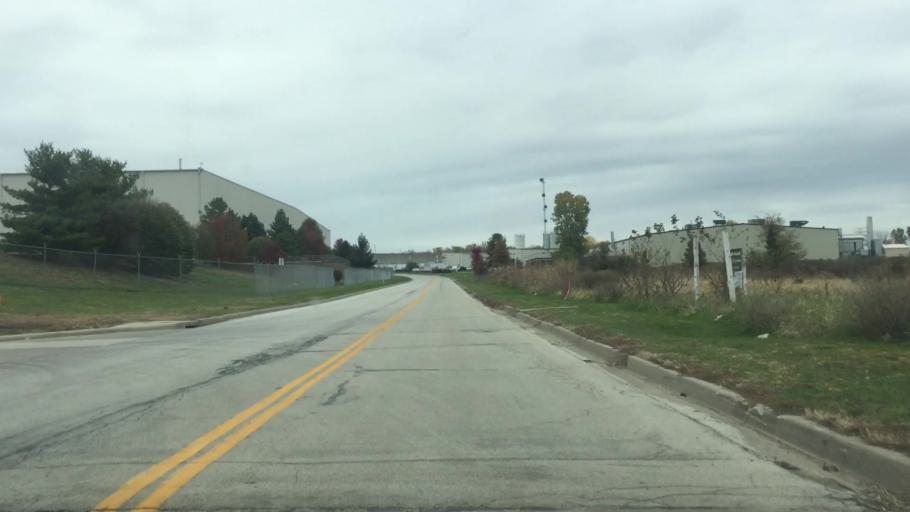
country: US
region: Missouri
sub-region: Jackson County
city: Lees Summit
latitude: 38.8825
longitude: -94.3628
